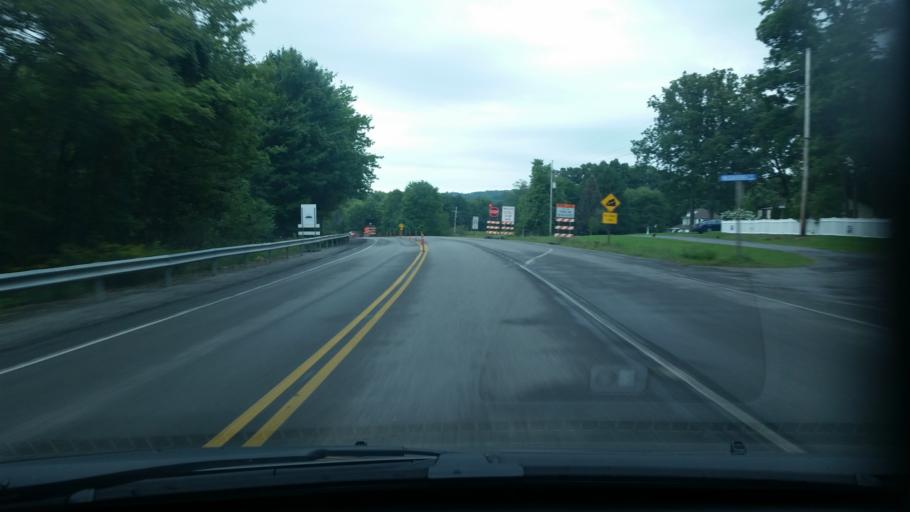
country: US
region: Pennsylvania
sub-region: Clearfield County
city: Shiloh
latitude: 41.0698
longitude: -78.3522
